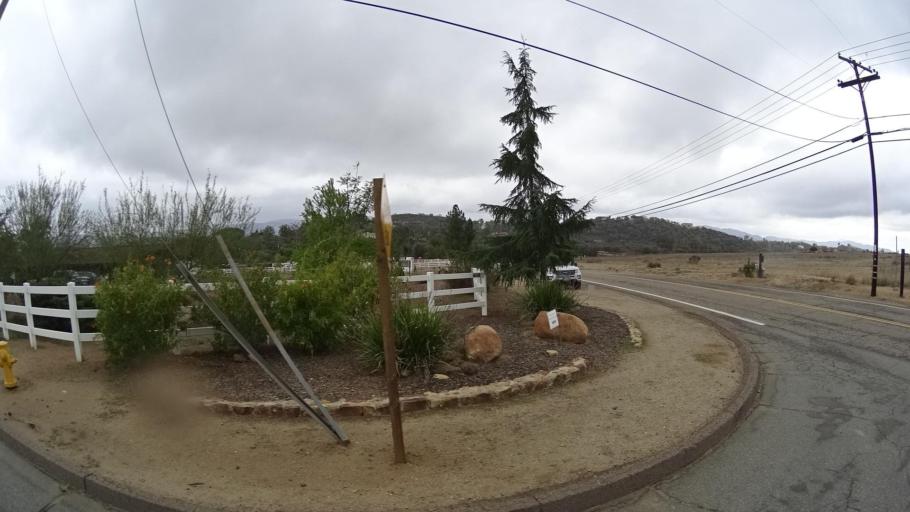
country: US
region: California
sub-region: San Diego County
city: Alpine
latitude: 32.8218
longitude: -116.7584
